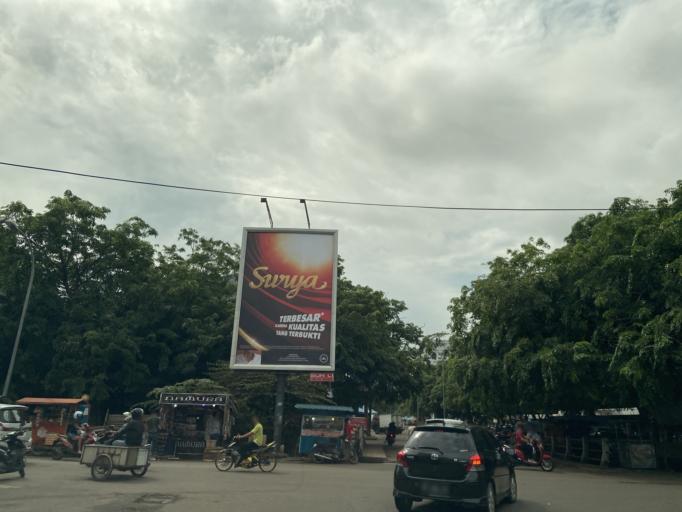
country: SG
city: Singapore
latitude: 1.1450
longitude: 104.0059
